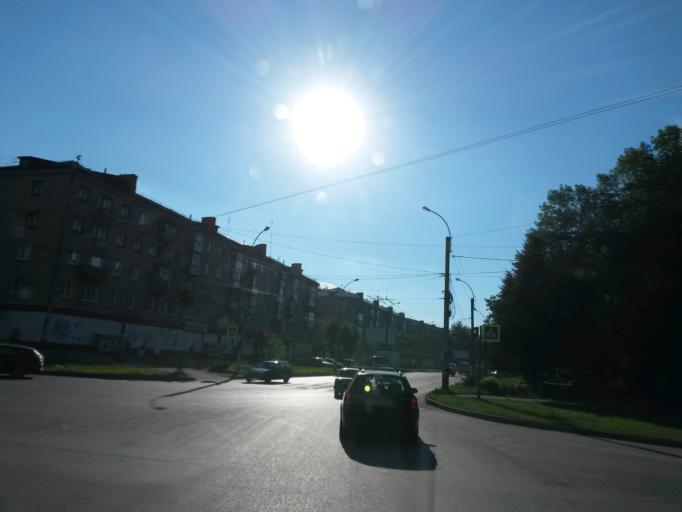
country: RU
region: Ivanovo
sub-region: Gorod Ivanovo
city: Ivanovo
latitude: 56.9829
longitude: 40.9683
